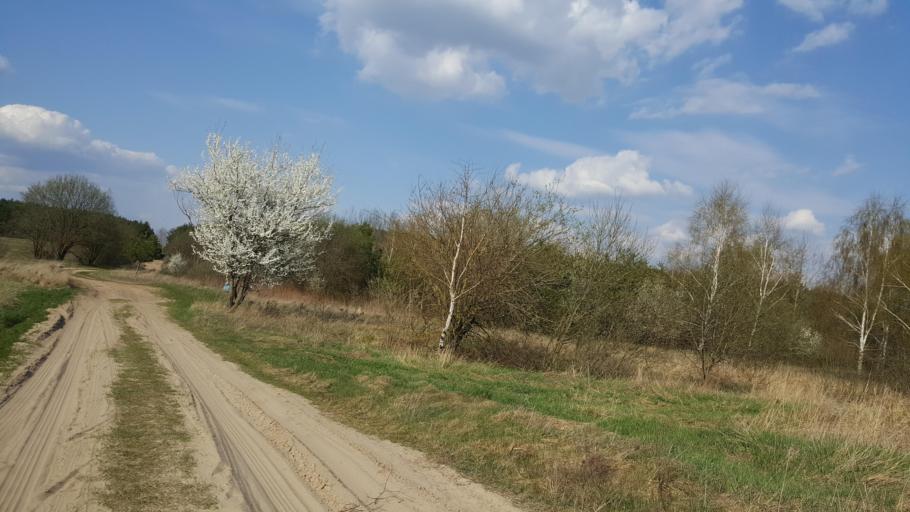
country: BY
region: Brest
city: Kamyanyets
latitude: 52.3757
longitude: 23.8378
